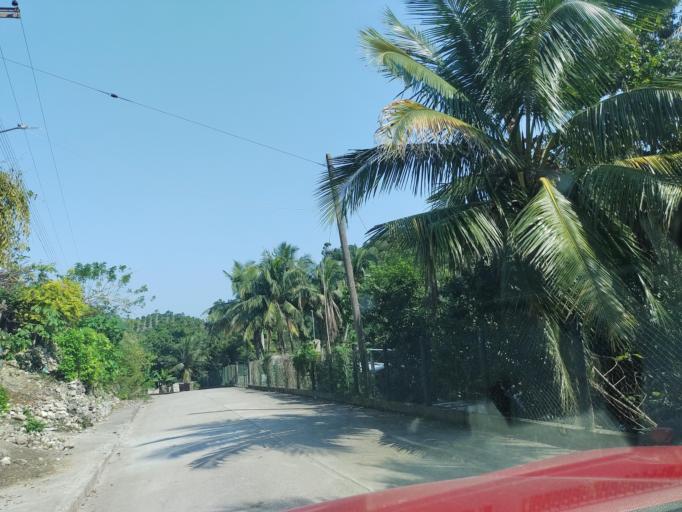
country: MX
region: Veracruz
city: Agua Dulce
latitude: 20.3367
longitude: -97.2018
